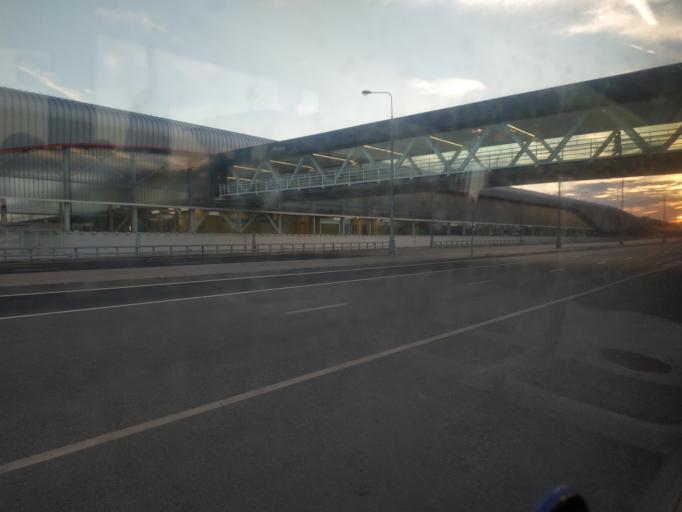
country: RU
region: Moscow
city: Solntsevo
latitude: 55.6012
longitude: 37.4091
